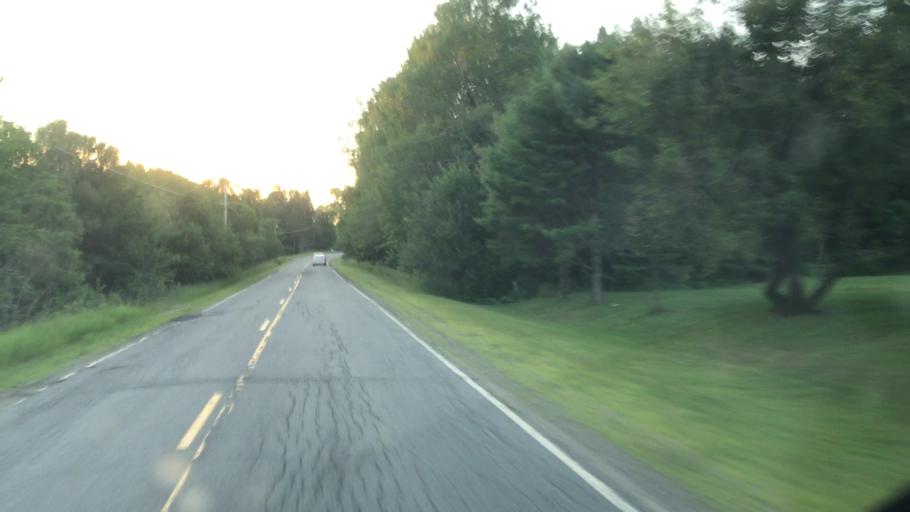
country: US
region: Maine
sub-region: Penobscot County
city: Medway
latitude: 45.5967
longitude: -68.2436
